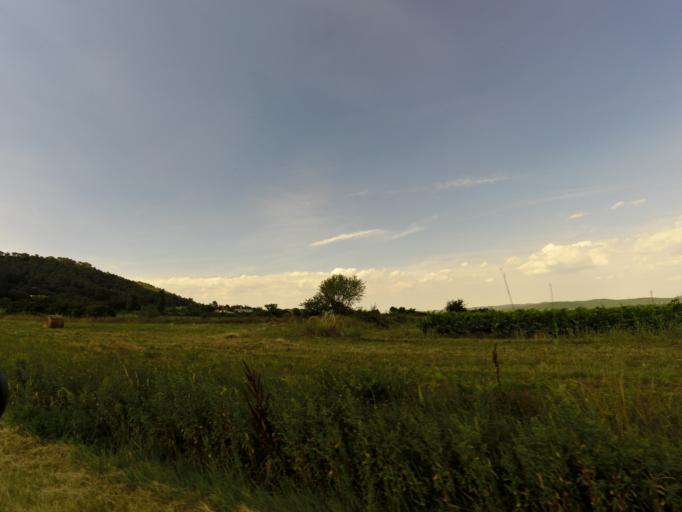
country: FR
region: Languedoc-Roussillon
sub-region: Departement du Gard
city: Sommieres
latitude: 43.8385
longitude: 4.0306
